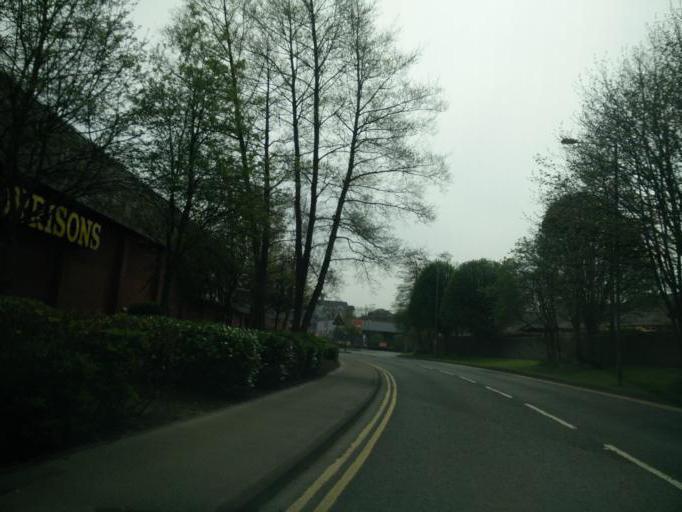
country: GB
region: England
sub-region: County Durham
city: Bishop Auckland
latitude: 54.6590
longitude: -1.6787
